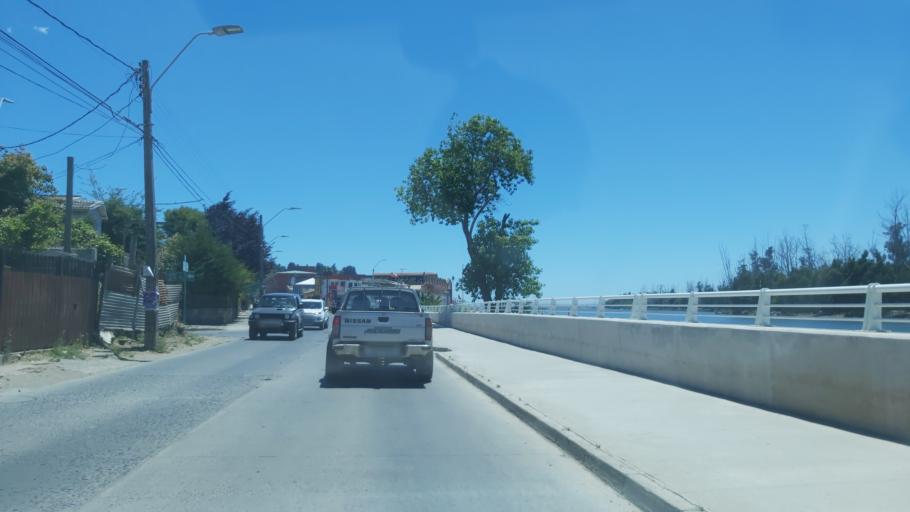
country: CL
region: Maule
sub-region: Provincia de Talca
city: Constitucion
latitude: -35.3329
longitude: -72.4059
